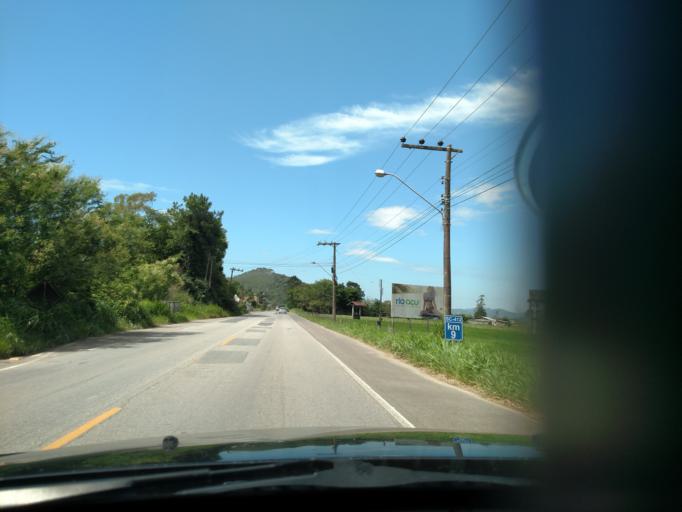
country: BR
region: Santa Catarina
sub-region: Itajai
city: Itajai
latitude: -26.8790
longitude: -48.7957
